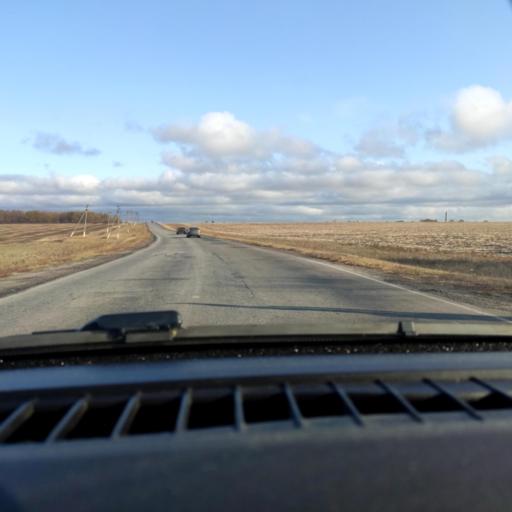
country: RU
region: Belgorod
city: Ilovka
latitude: 50.7174
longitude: 38.6743
